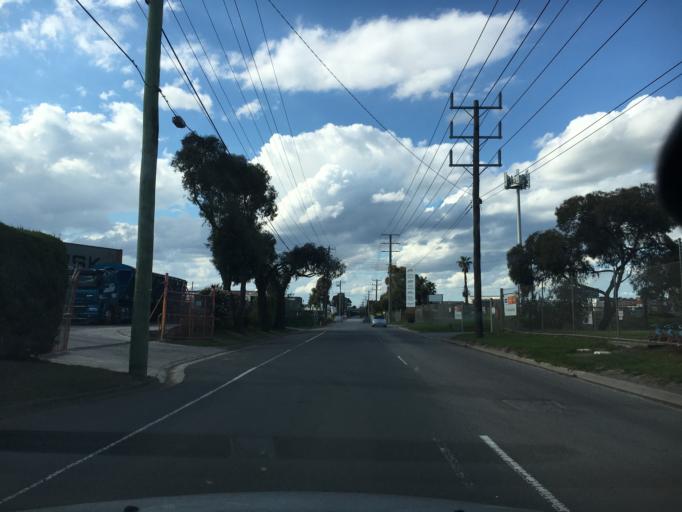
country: AU
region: Victoria
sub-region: Monash
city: Clayton
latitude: -37.9235
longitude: 145.1459
